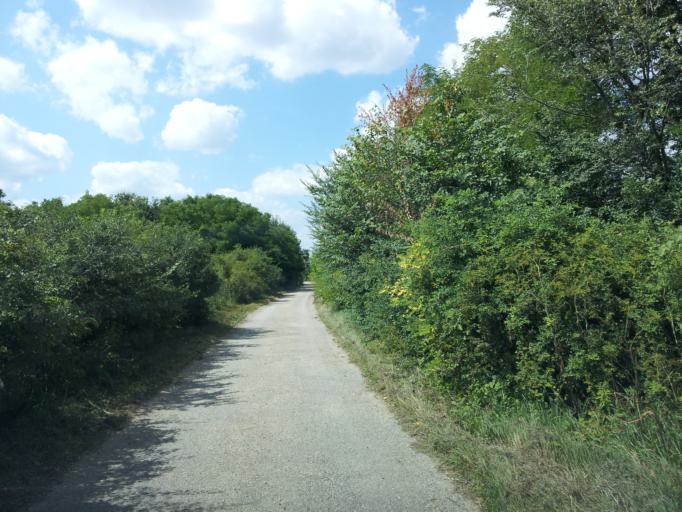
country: HU
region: Veszprem
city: Balatonkenese
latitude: 47.0520
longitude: 18.0704
